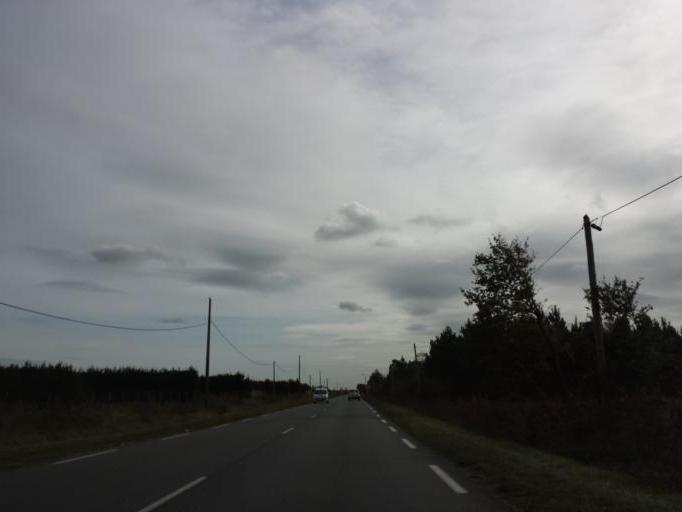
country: FR
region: Aquitaine
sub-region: Departement de la Gironde
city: Marcheprime
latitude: 44.7737
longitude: -0.9282
